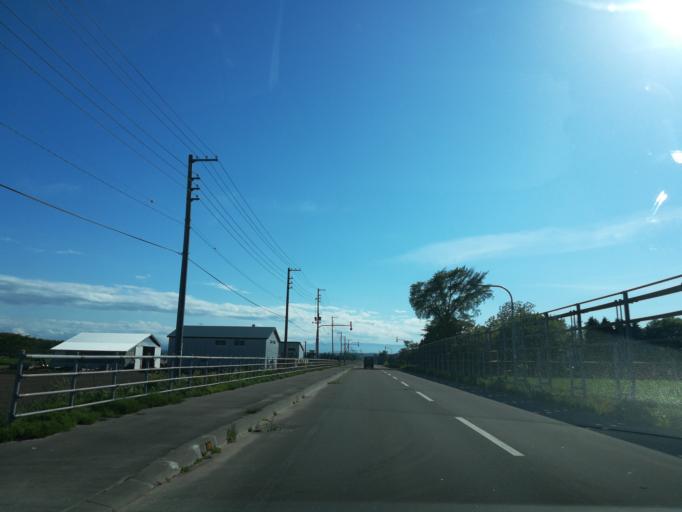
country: JP
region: Hokkaido
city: Ebetsu
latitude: 43.0531
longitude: 141.6091
